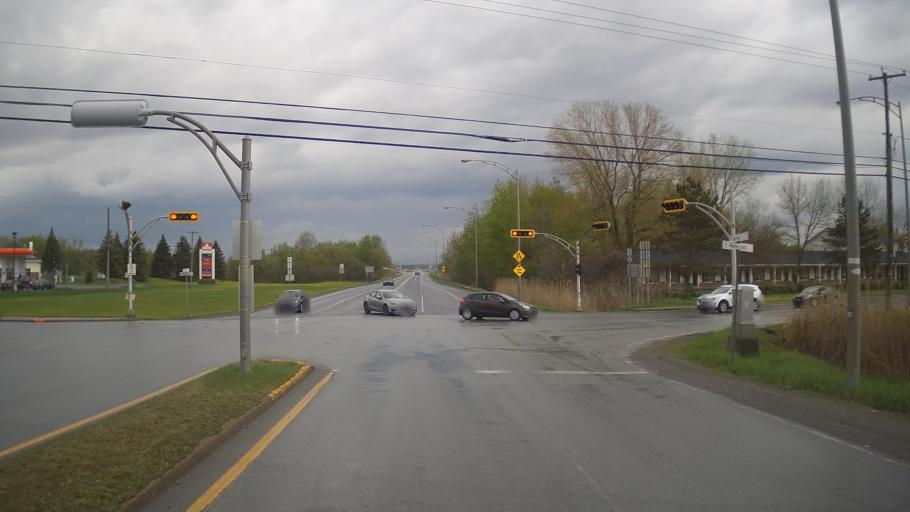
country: CA
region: Quebec
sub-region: Monteregie
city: Farnham
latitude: 45.2868
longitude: -72.9927
